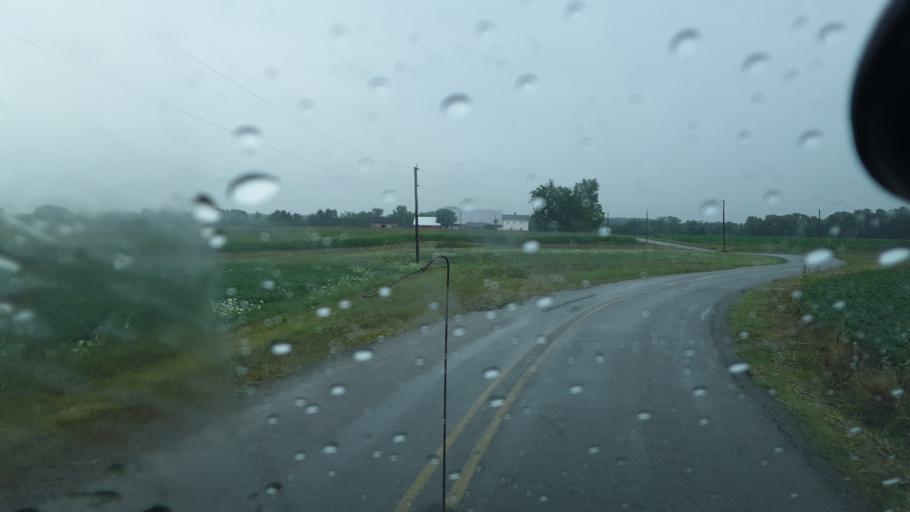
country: US
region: Indiana
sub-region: DeKalb County
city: Butler
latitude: 41.4454
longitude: -84.8134
